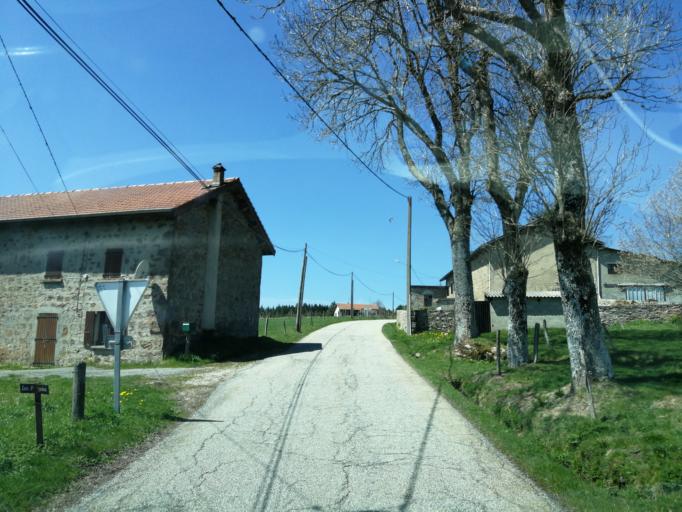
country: FR
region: Auvergne
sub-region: Departement de la Haute-Loire
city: Riotord
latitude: 45.1217
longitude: 4.4078
